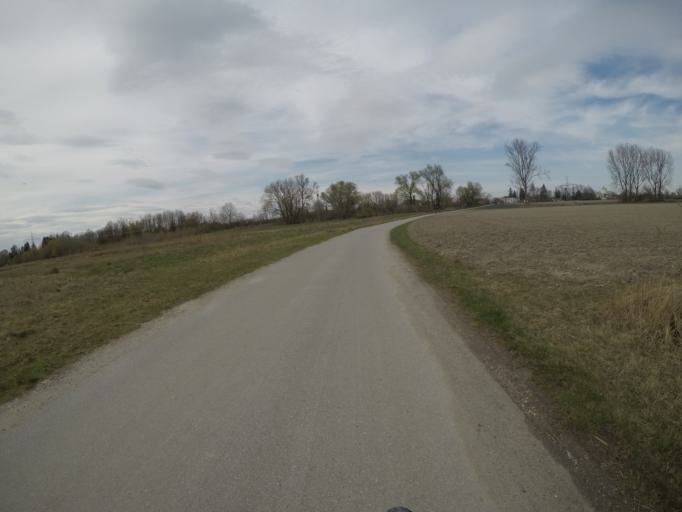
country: DE
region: Bavaria
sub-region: Lower Bavaria
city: Essenbach
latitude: 48.5885
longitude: 12.2304
